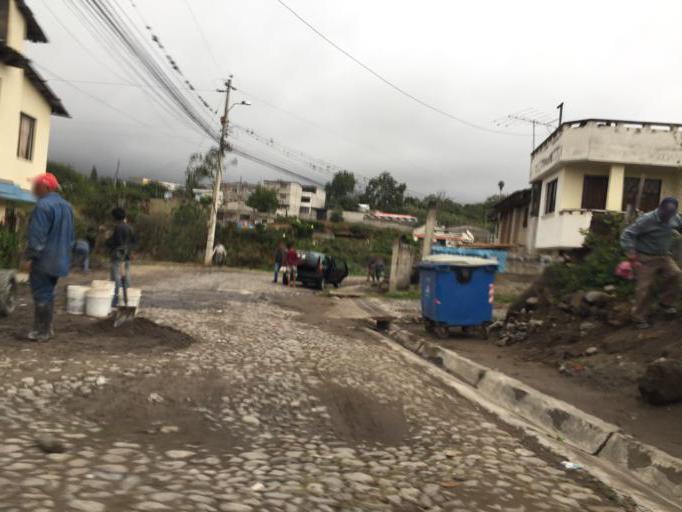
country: EC
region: Imbabura
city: Atuntaqui
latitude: 0.3376
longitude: -78.1718
